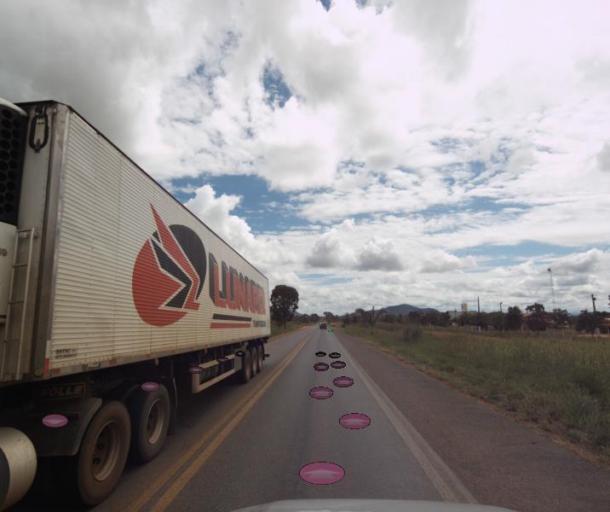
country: BR
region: Goias
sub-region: Uruacu
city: Uruacu
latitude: -14.4663
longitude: -49.1561
